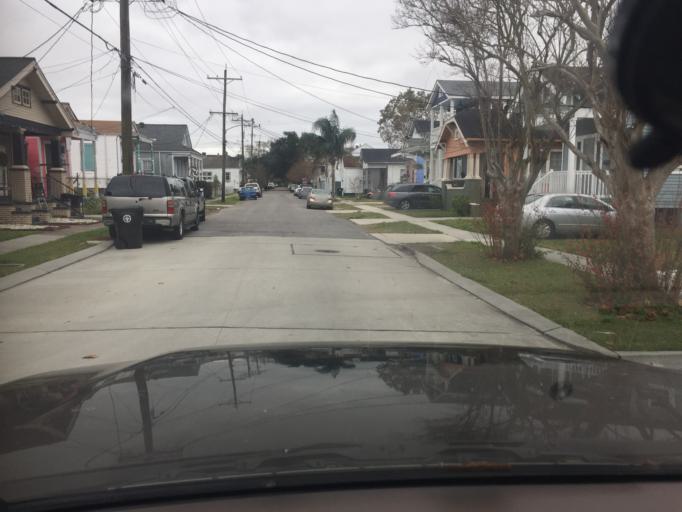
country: US
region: Louisiana
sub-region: Orleans Parish
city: New Orleans
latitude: 29.9830
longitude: -90.0751
